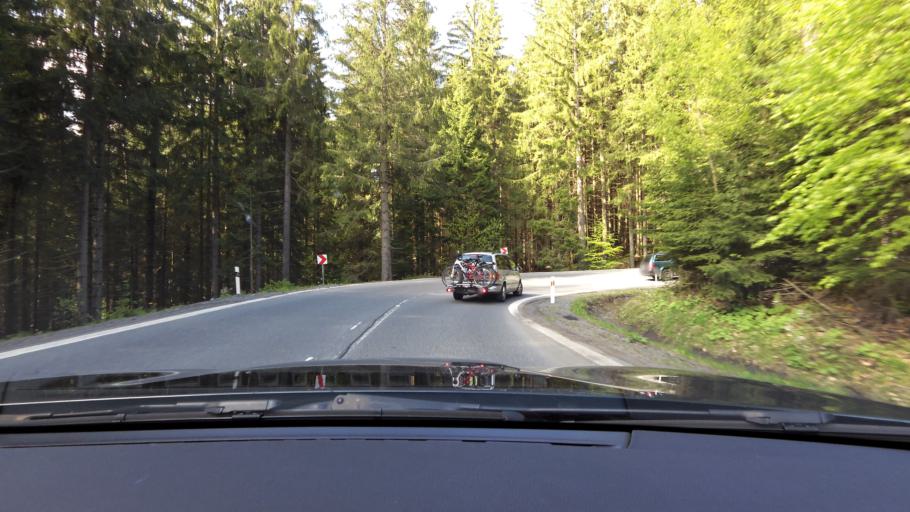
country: CZ
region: Plzensky
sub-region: Okres Klatovy
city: Zelezna Ruda
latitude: 49.2101
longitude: 13.3074
